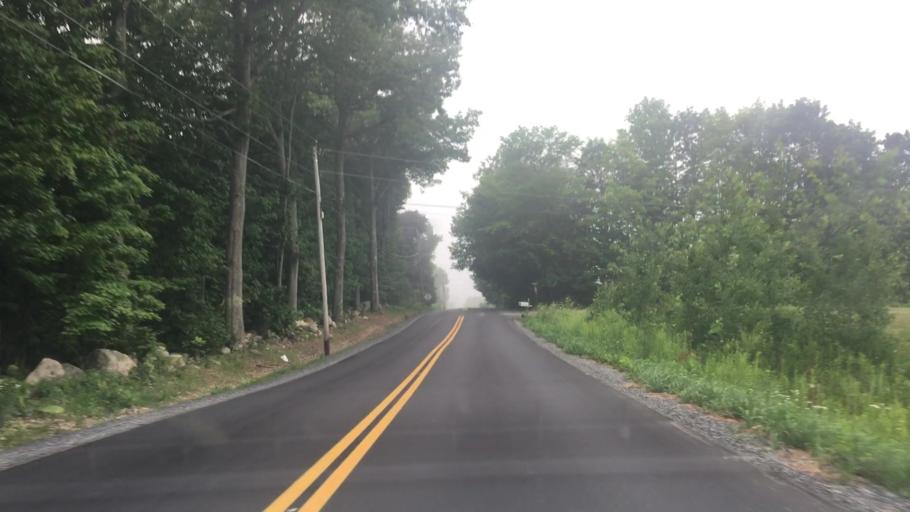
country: US
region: Maine
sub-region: Kennebec County
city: Oakland
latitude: 44.5165
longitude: -69.7170
